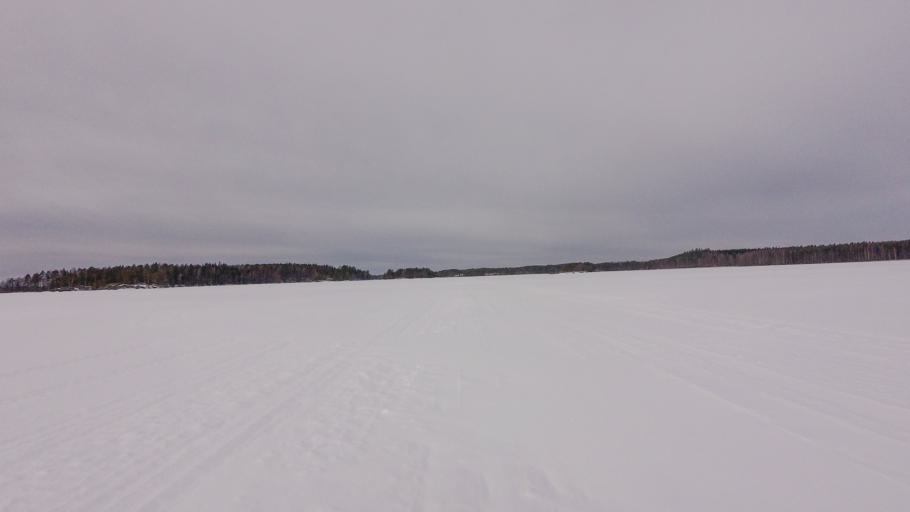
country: FI
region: Southern Savonia
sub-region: Savonlinna
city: Rantasalmi
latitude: 62.1138
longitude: 28.3692
